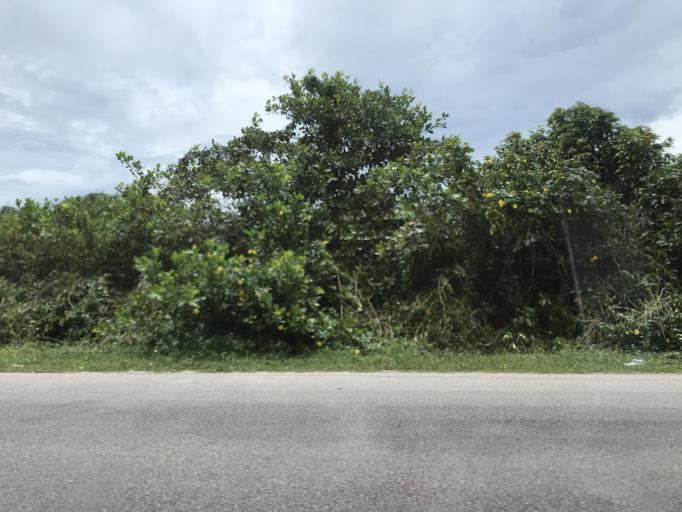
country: MY
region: Kelantan
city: Tumpat
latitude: 6.1785
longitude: 102.1833
